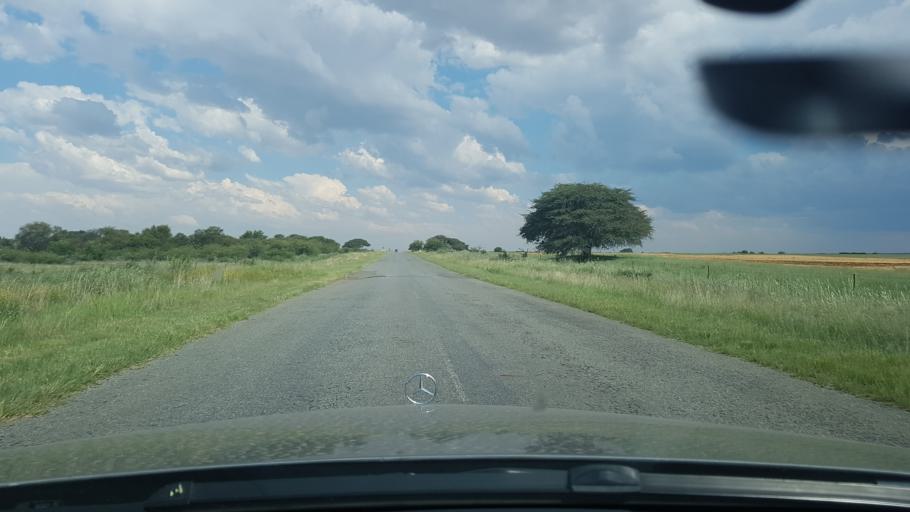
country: ZA
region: North-West
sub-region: Dr Ruth Segomotsi Mompati District Municipality
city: Bloemhof
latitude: -27.8076
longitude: 25.6237
